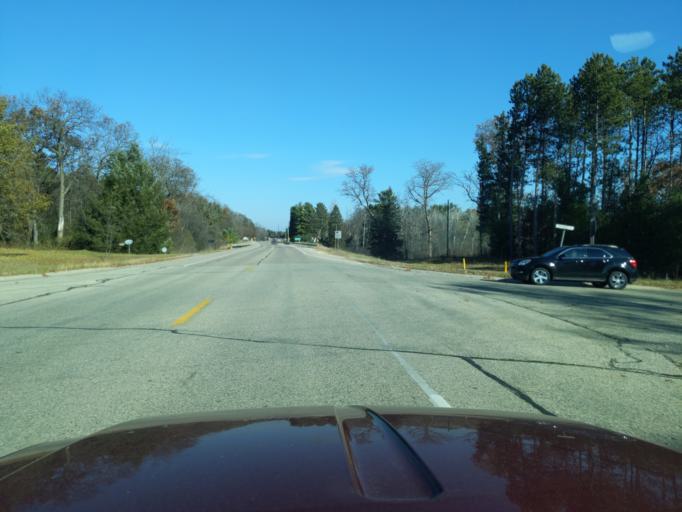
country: US
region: Wisconsin
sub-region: Waushara County
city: Wautoma
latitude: 44.0475
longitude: -89.2953
